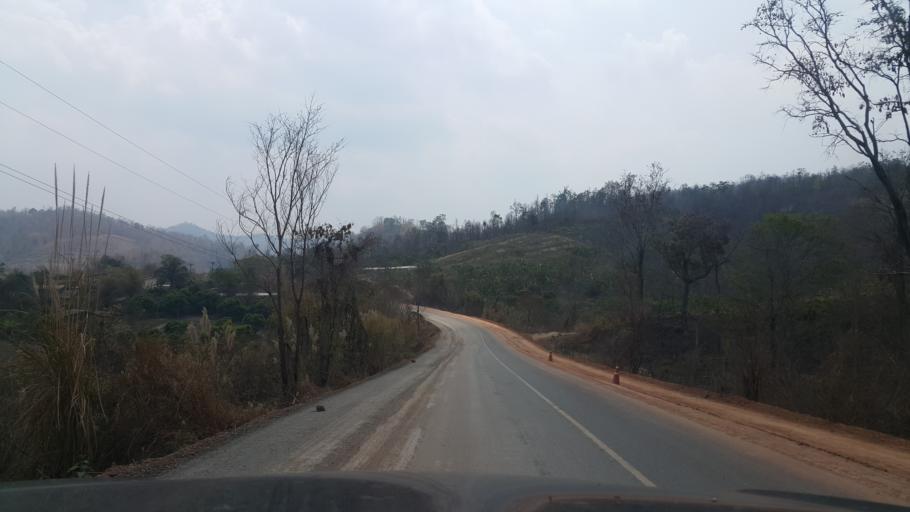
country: TH
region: Lamphun
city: Thung Hua Chang
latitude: 18.1954
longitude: 98.9737
